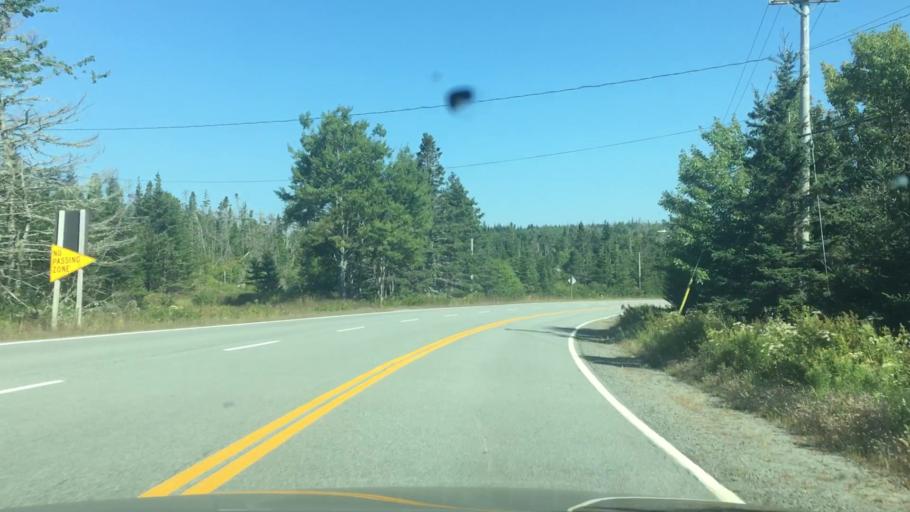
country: CA
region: Nova Scotia
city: New Glasgow
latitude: 44.8125
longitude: -62.6410
